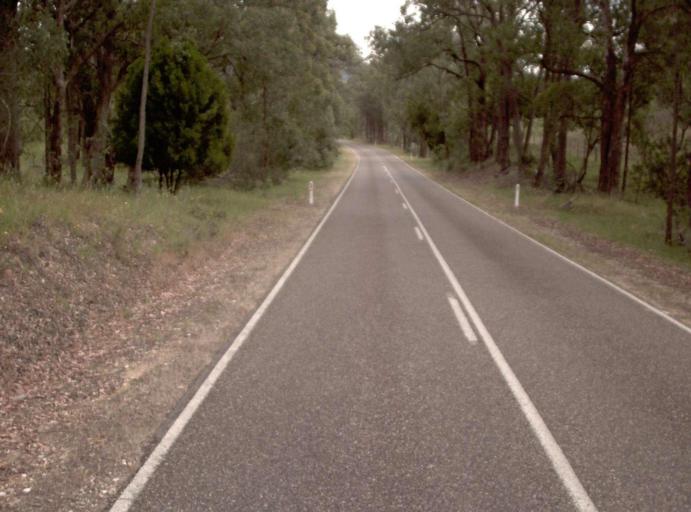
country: AU
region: Victoria
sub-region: East Gippsland
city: Bairnsdale
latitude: -37.7848
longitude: 147.3242
